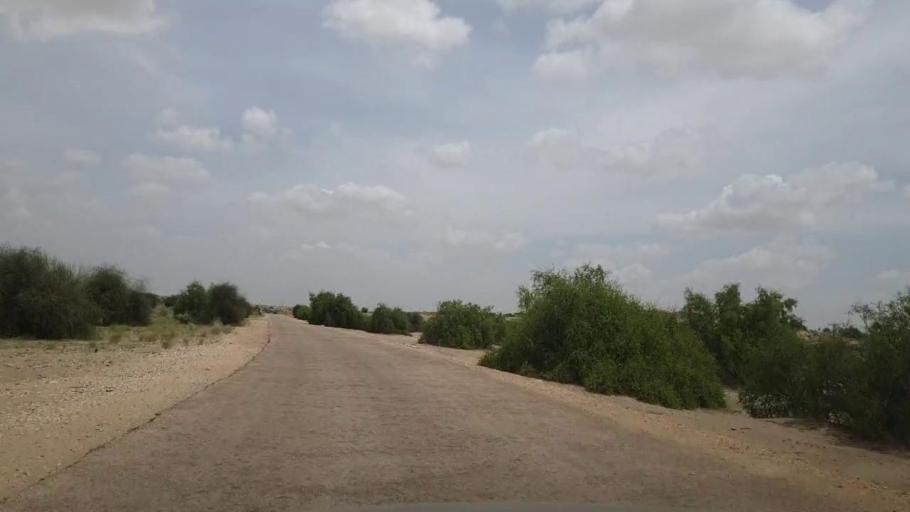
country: PK
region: Sindh
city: Kot Diji
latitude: 27.1968
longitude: 69.1582
